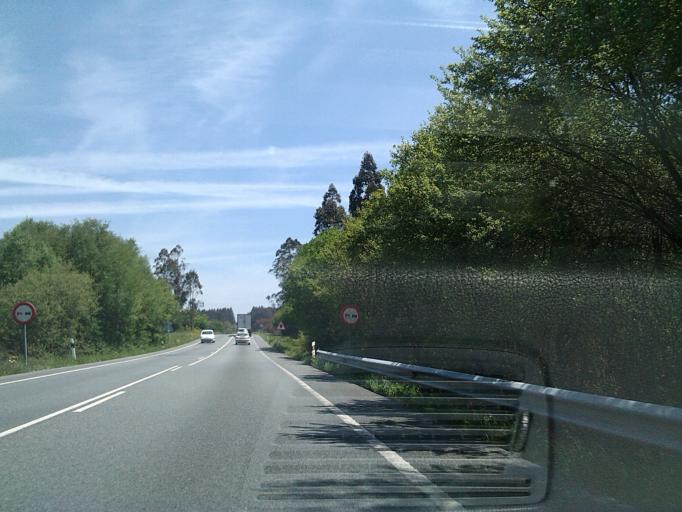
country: ES
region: Galicia
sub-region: Provincia da Coruna
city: Curtis
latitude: 43.1196
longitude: -8.0843
